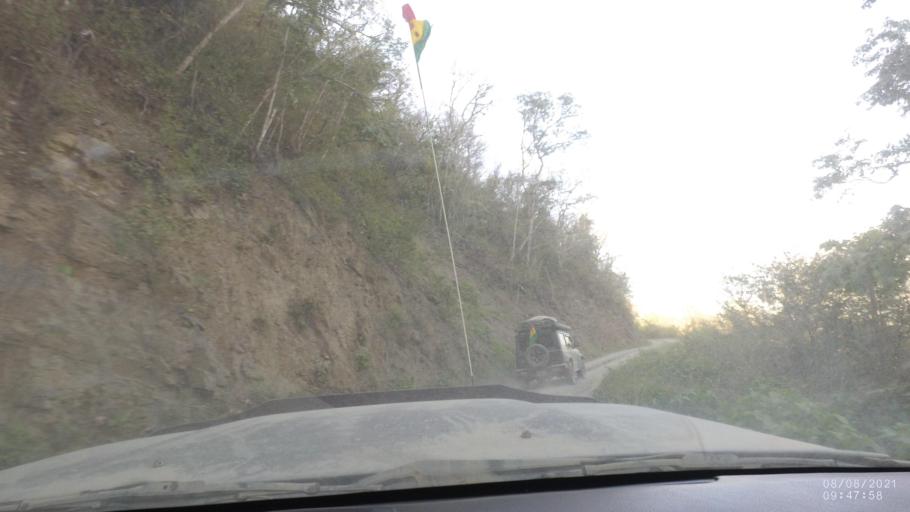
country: BO
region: La Paz
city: Quime
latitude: -16.6108
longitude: -66.7286
